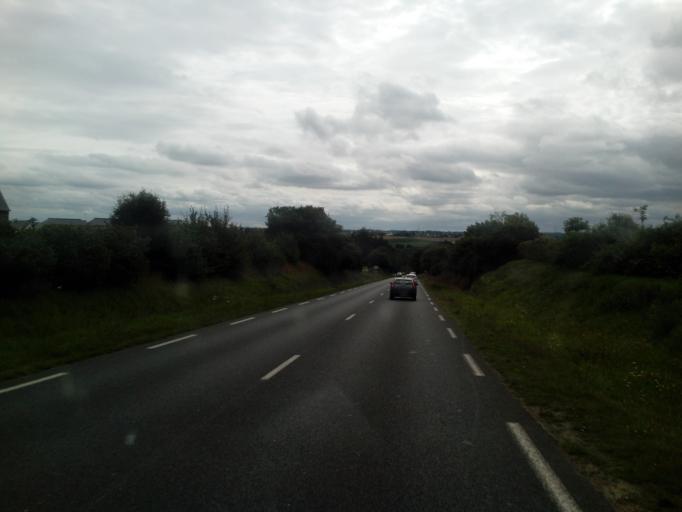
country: FR
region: Brittany
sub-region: Departement des Cotes-d'Armor
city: Binic
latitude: 48.6083
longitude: -2.8347
